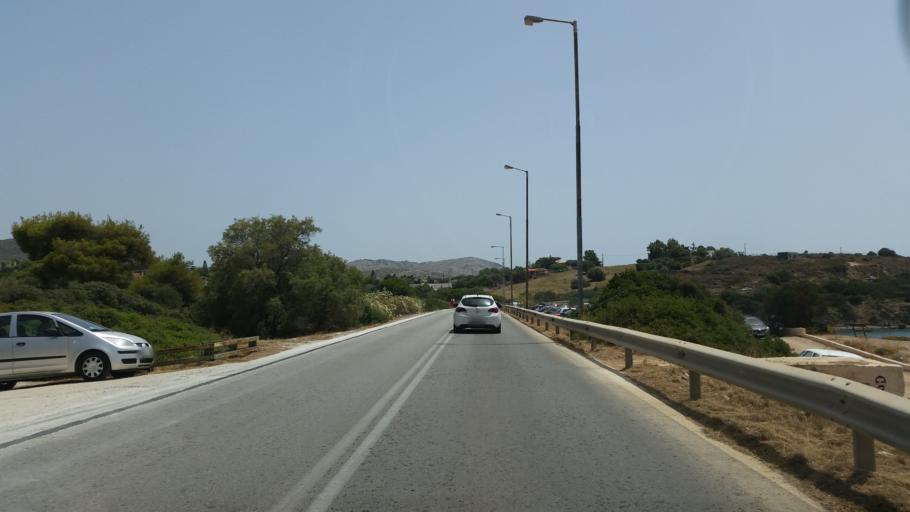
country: GR
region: Attica
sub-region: Nomarchia Anatolikis Attikis
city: Palaia Fokaia
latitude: 37.7024
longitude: 23.9401
